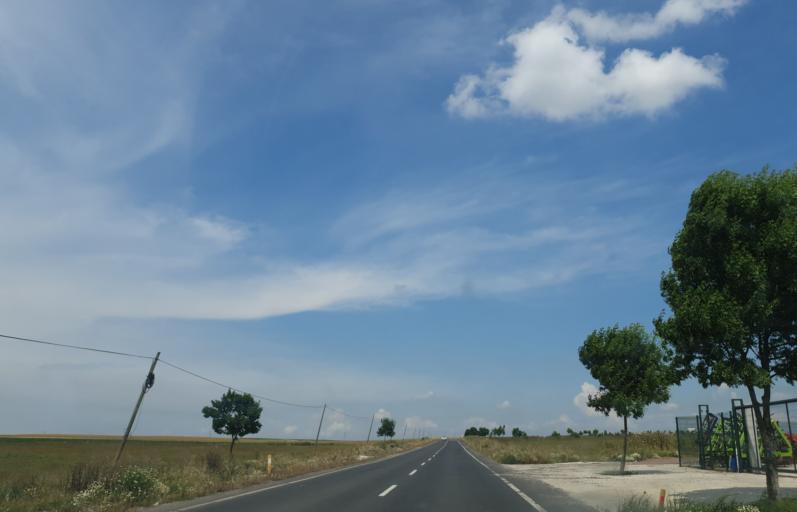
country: TR
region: Kirklareli
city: Buyukkaristiran
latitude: 41.2431
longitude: 27.6012
